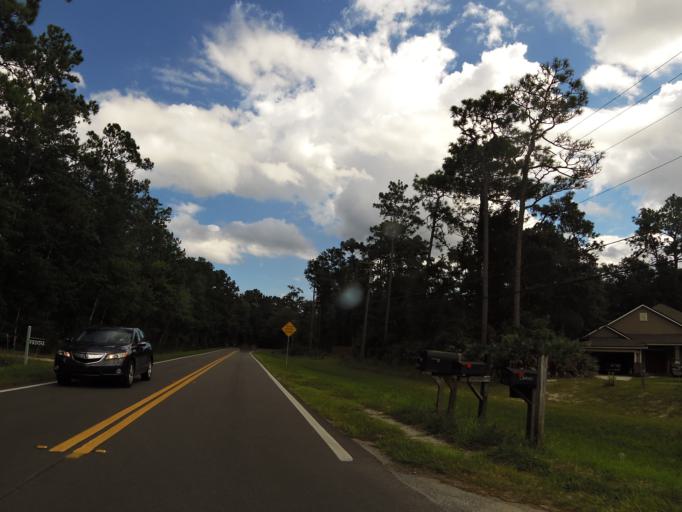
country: US
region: Florida
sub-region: Saint Johns County
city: Saint Augustine
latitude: 29.9122
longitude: -81.4946
